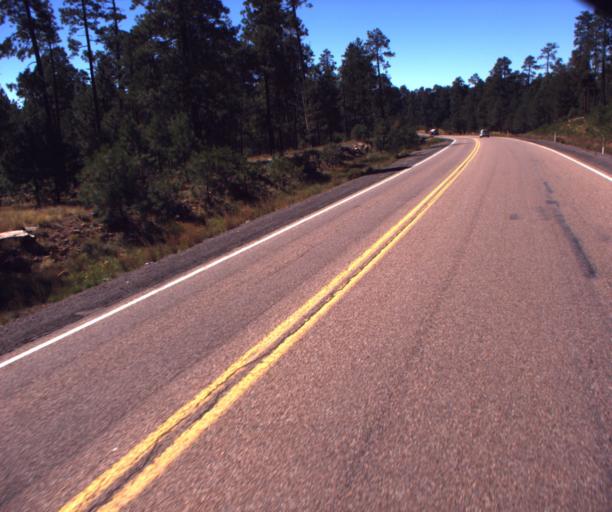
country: US
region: Arizona
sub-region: Navajo County
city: Heber-Overgaard
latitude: 34.3251
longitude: -110.8361
